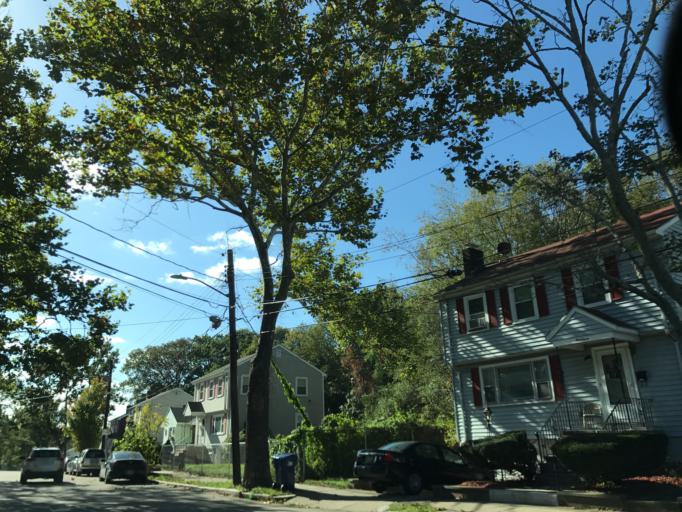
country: US
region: Massachusetts
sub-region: Norfolk County
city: Milton
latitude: 42.2758
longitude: -71.0784
